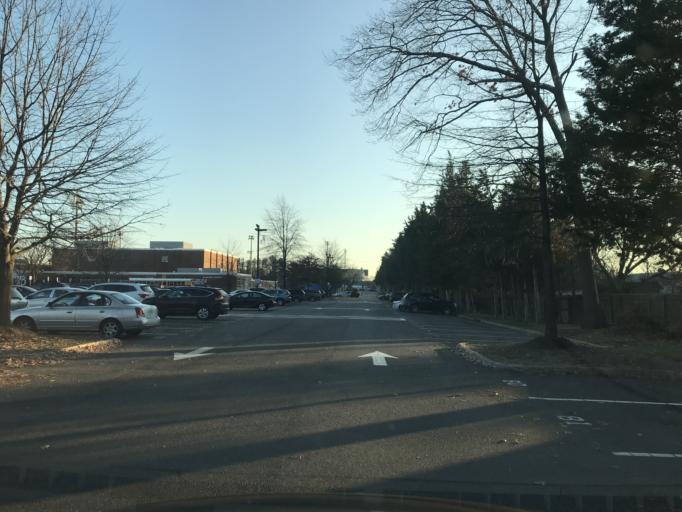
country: US
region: Virginia
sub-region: Fairfax County
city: Springfield
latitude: 38.7810
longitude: -77.1711
